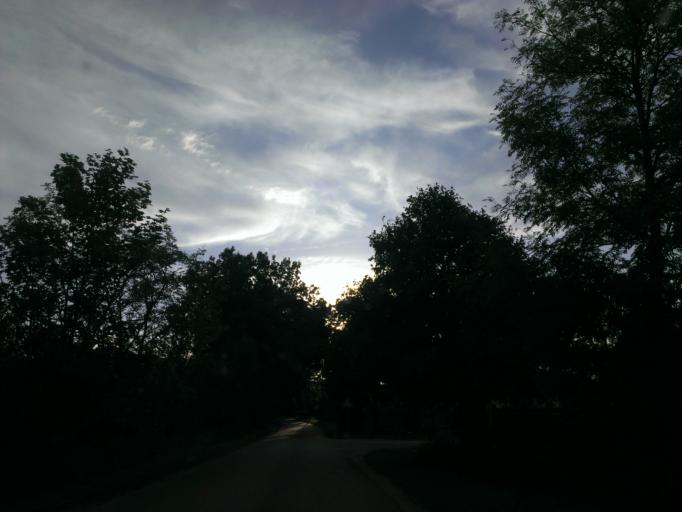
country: LV
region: Ikskile
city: Ikskile
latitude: 56.8403
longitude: 24.5117
